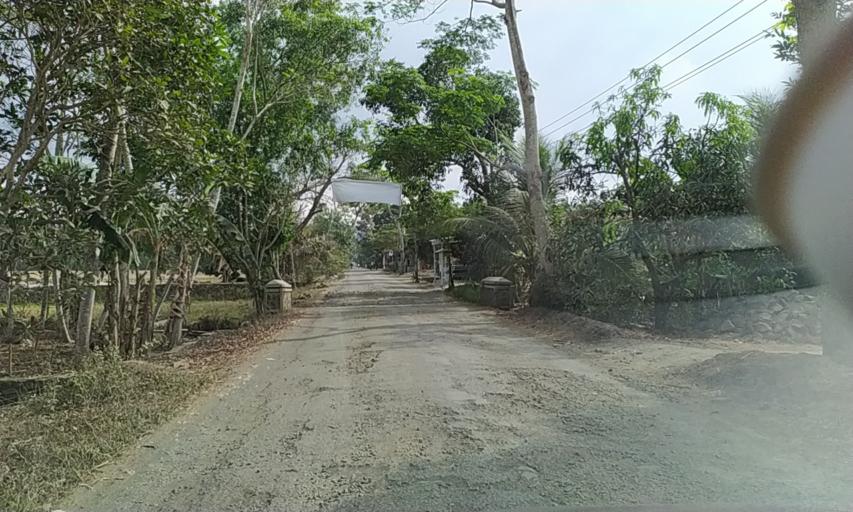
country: ID
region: Central Java
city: Sawoan
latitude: -7.6226
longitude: 109.0518
